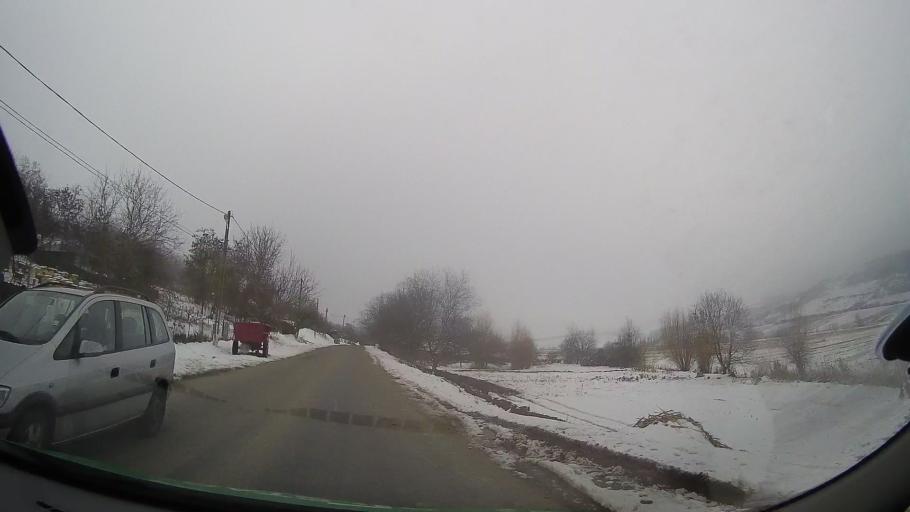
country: RO
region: Bacau
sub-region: Comuna Vultureni
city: Vultureni
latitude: 46.3487
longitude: 27.2892
